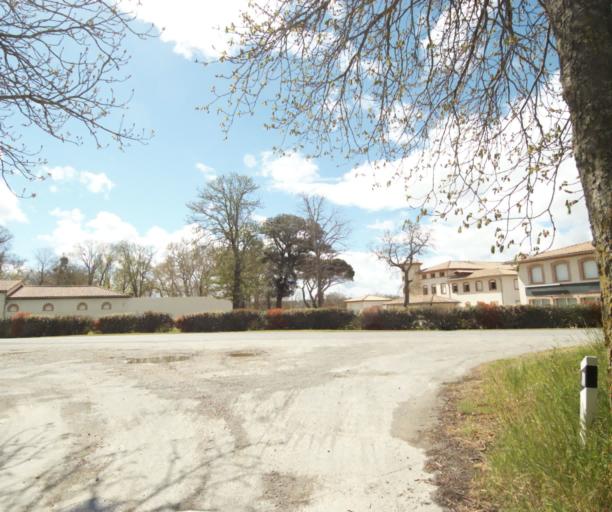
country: FR
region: Midi-Pyrenees
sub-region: Departement de l'Ariege
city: Saverdun
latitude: 43.2301
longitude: 1.6018
